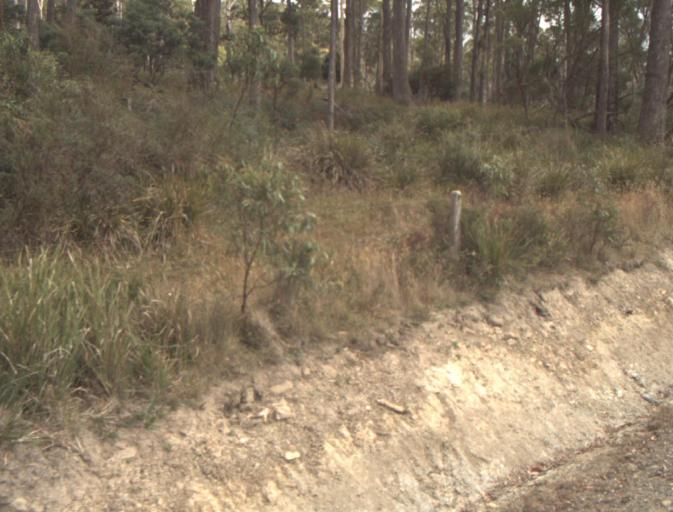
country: AU
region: Tasmania
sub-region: Northern Midlands
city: Evandale
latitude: -41.4661
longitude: 147.4481
